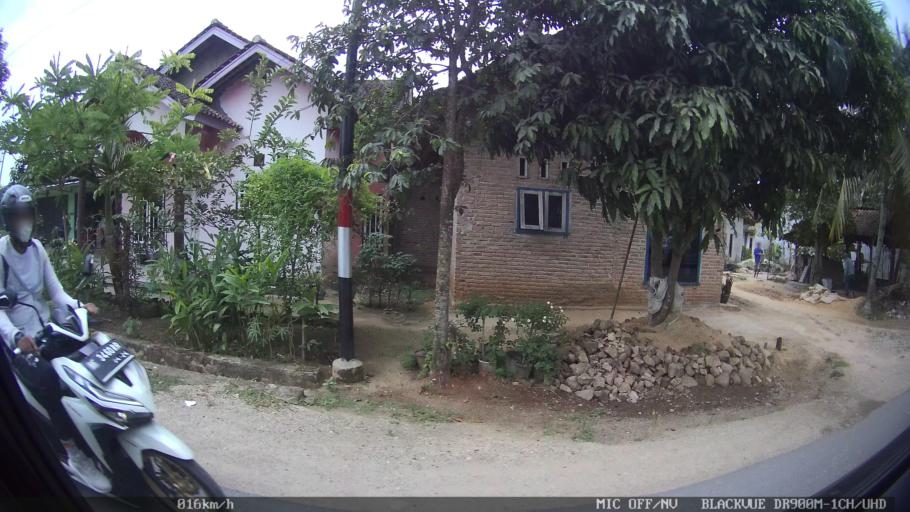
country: ID
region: Lampung
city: Gadingrejo
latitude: -5.3846
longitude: 105.0424
